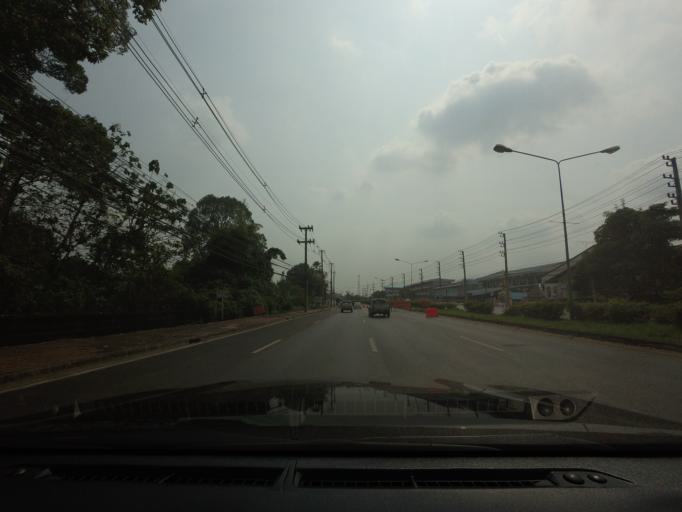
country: TH
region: Nakhon Nayok
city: Nakhon Nayok
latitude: 14.2027
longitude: 101.2183
